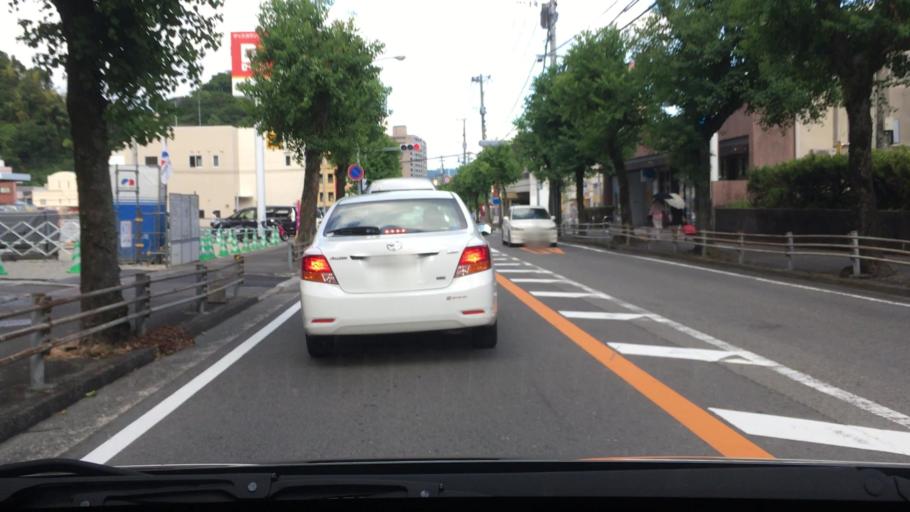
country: JP
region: Nagasaki
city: Togitsu
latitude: 32.8077
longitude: 129.8361
